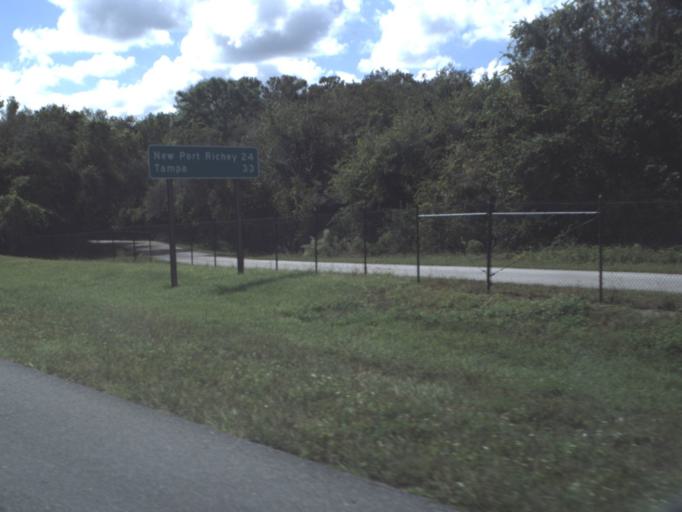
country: US
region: Florida
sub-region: Pasco County
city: Shady Hills
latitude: 28.3157
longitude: -82.5512
